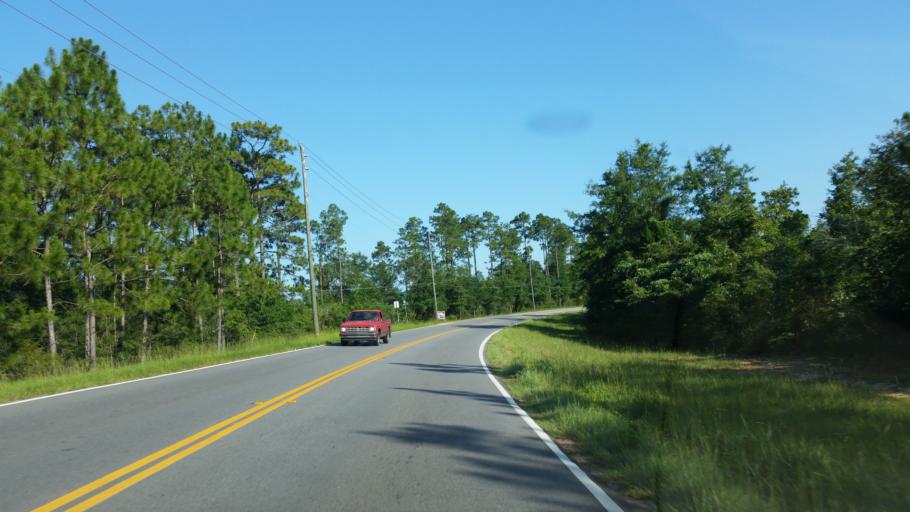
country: US
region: Florida
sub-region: Escambia County
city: Cantonment
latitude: 30.5572
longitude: -87.3806
